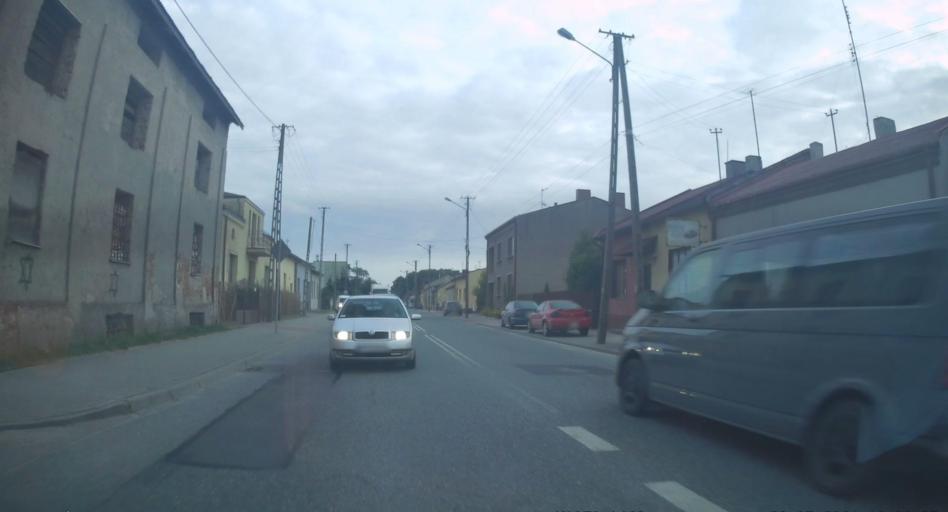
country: PL
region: Lodz Voivodeship
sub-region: Powiat radomszczanski
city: Kamiensk
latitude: 51.1933
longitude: 19.4984
